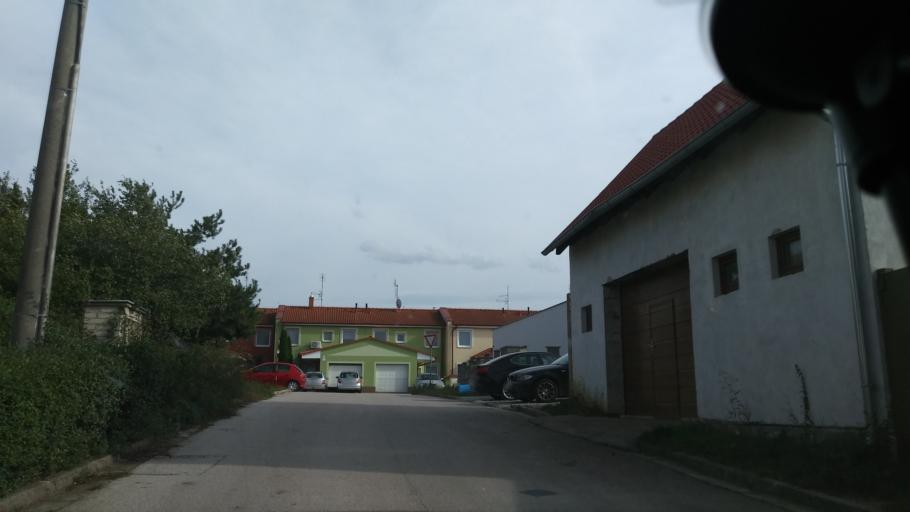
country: SK
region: Trnavsky
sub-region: Okres Skalica
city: Skalica
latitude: 48.8492
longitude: 17.2408
